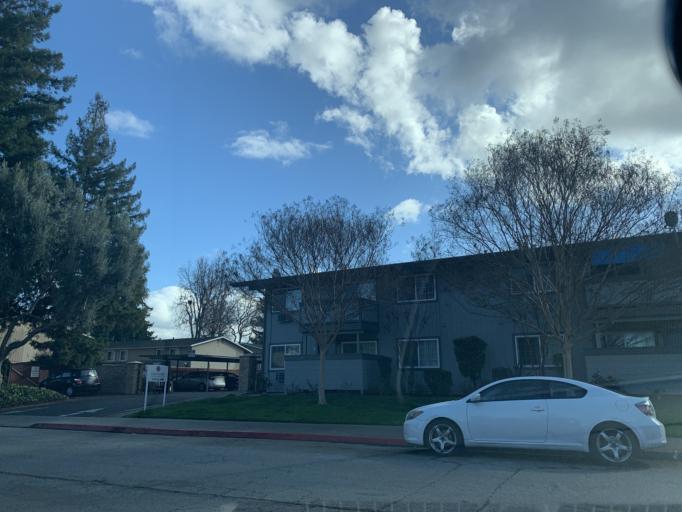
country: US
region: California
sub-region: Santa Clara County
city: Buena Vista
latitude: 37.3014
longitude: -121.9258
